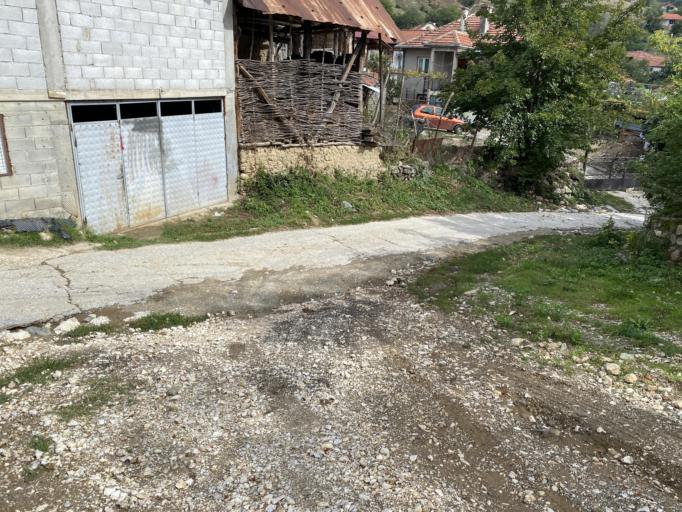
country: MK
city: Radishani
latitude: 42.1096
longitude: 21.4542
